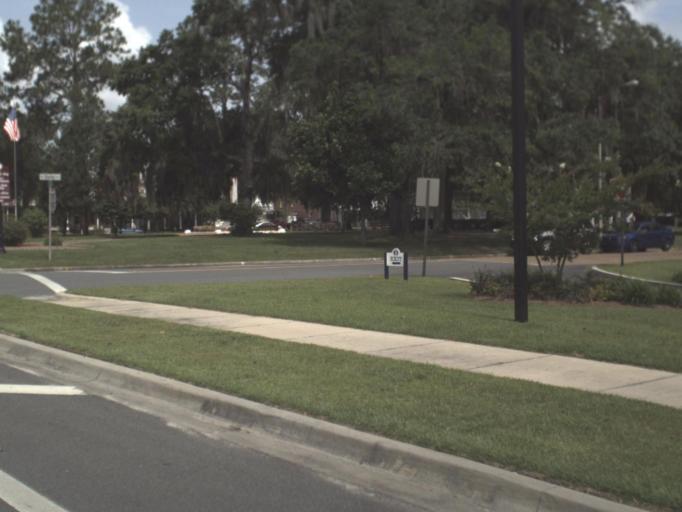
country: US
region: Florida
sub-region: Madison County
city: Madison
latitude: 30.4695
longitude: -83.4117
